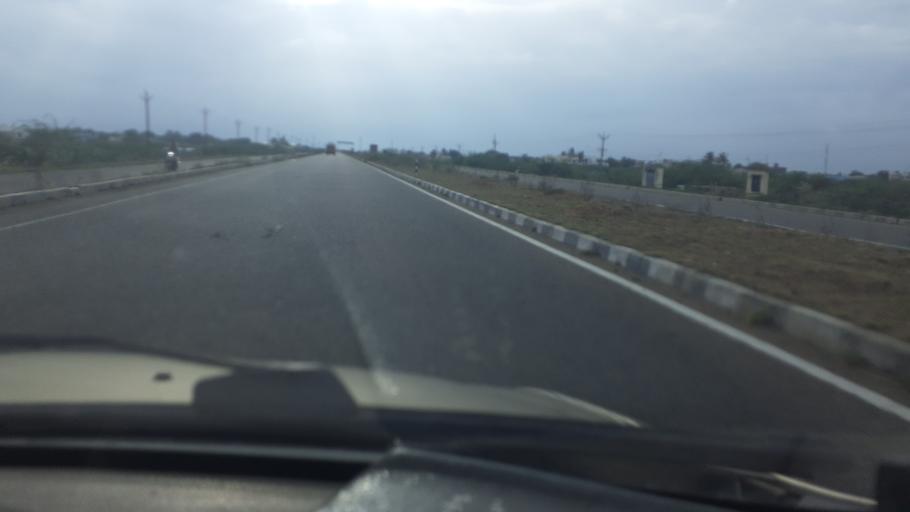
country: IN
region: Tamil Nadu
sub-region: Tirunelveli Kattabo
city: Tirunelveli
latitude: 8.6632
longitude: 77.7277
